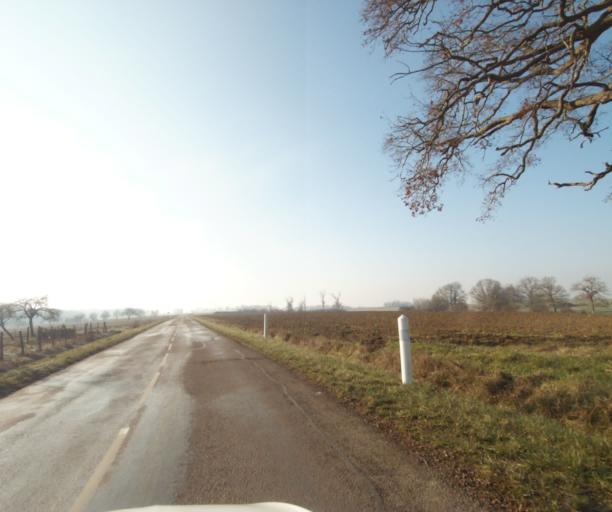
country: FR
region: Champagne-Ardenne
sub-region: Departement de la Haute-Marne
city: Montier-en-Der
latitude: 48.4424
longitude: 4.7578
